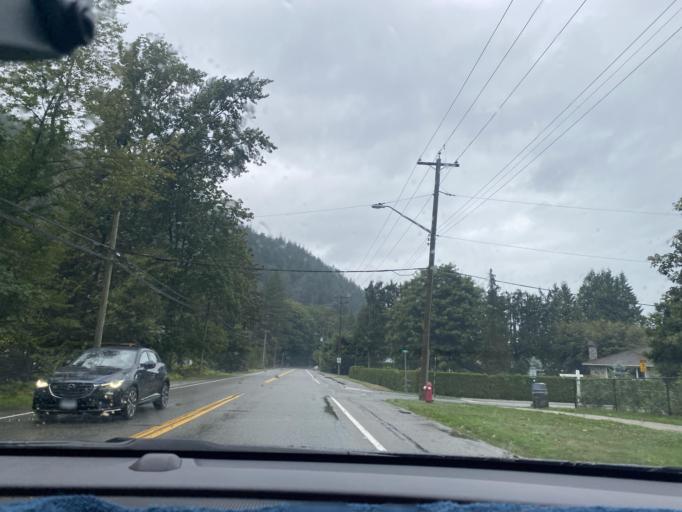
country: CA
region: British Columbia
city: Agassiz
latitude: 49.2936
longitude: -121.7817
